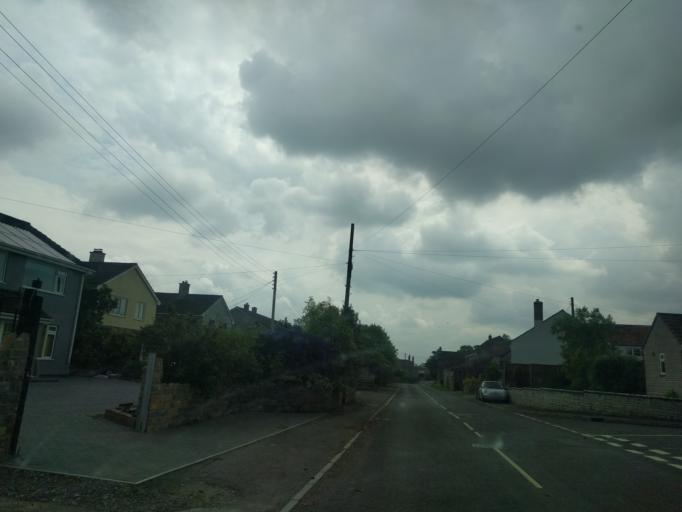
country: GB
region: England
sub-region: Somerset
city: Langport
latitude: 51.0785
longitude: -2.8213
